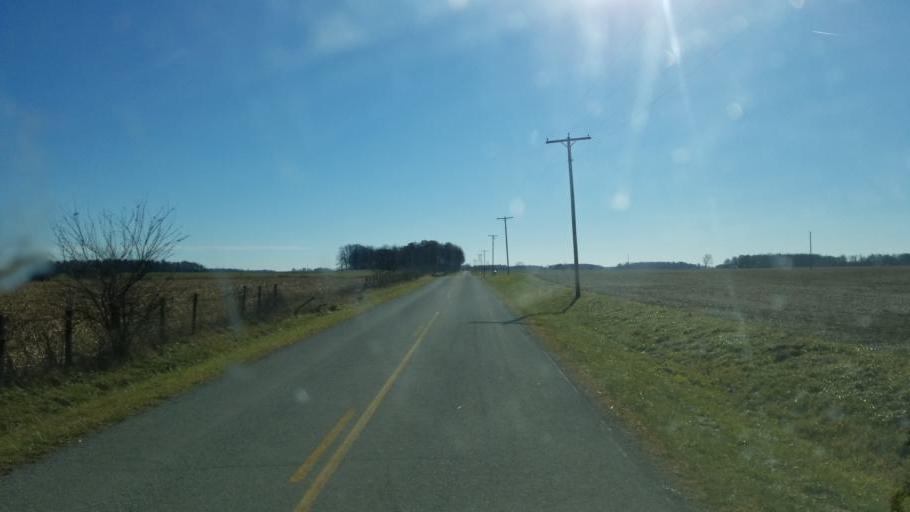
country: US
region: Ohio
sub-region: Crawford County
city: Crestline
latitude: 40.8349
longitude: -82.8375
